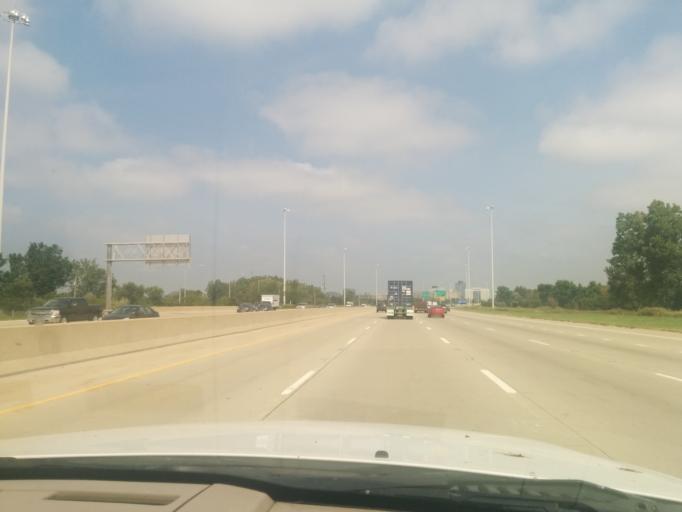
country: US
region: Illinois
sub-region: DuPage County
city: Itasca
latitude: 42.0129
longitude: -88.0301
